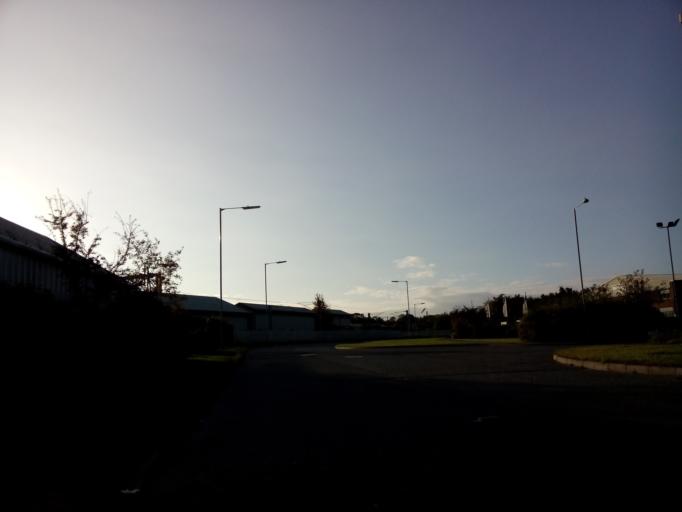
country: GB
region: England
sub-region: Suffolk
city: Bramford
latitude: 52.0667
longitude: 1.1153
